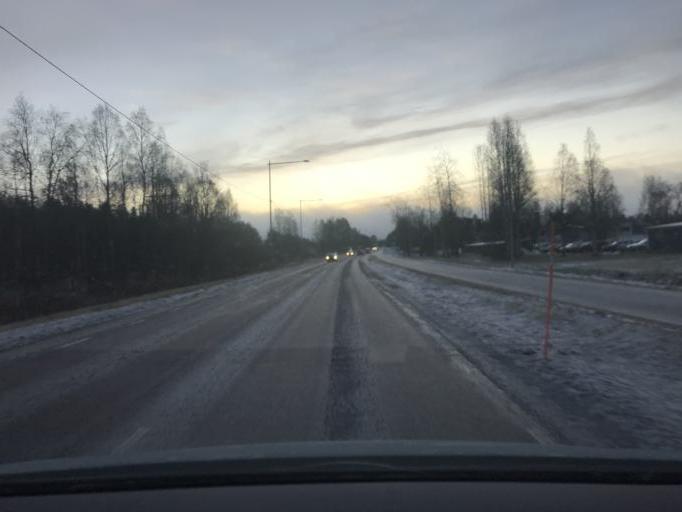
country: SE
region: Norrbotten
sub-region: Lulea Kommun
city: Gammelstad
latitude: 65.6369
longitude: 22.0274
